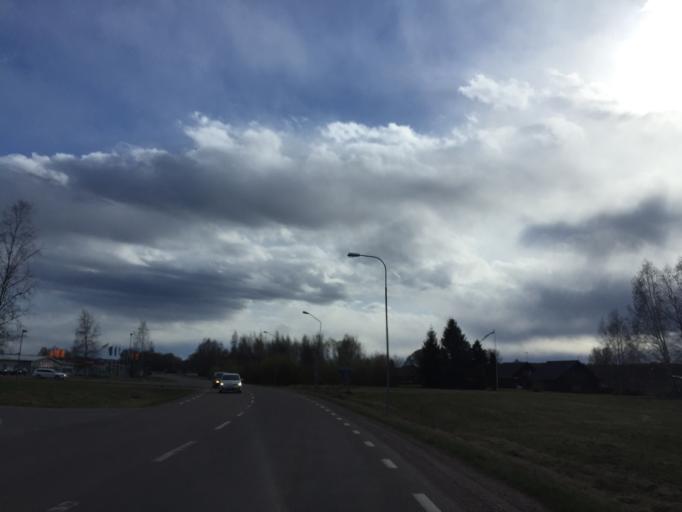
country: SE
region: Dalarna
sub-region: Borlange Kommun
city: Borlaenge
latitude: 60.4780
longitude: 15.4063
